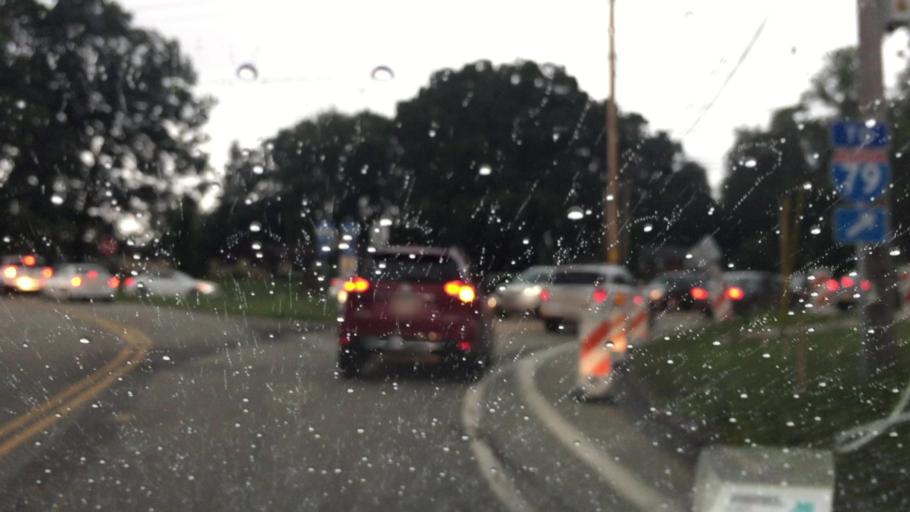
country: US
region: Pennsylvania
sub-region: Allegheny County
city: Franklin Park
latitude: 40.5533
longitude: -80.1057
